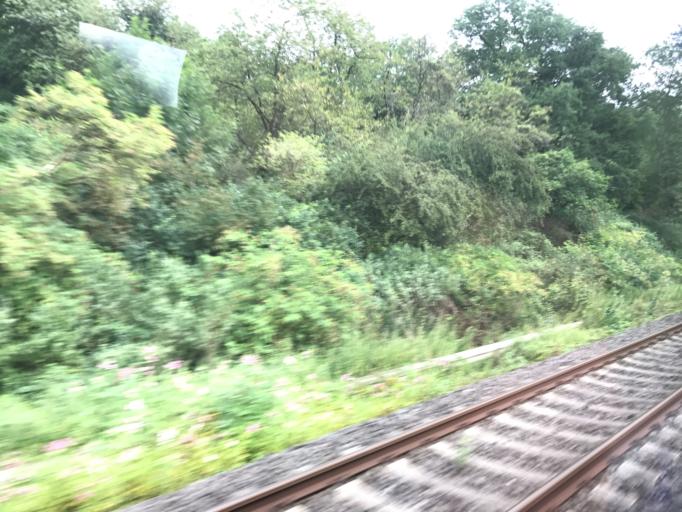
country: DE
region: Hesse
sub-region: Regierungsbezirk Giessen
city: Villmar
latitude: 50.3952
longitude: 8.1732
